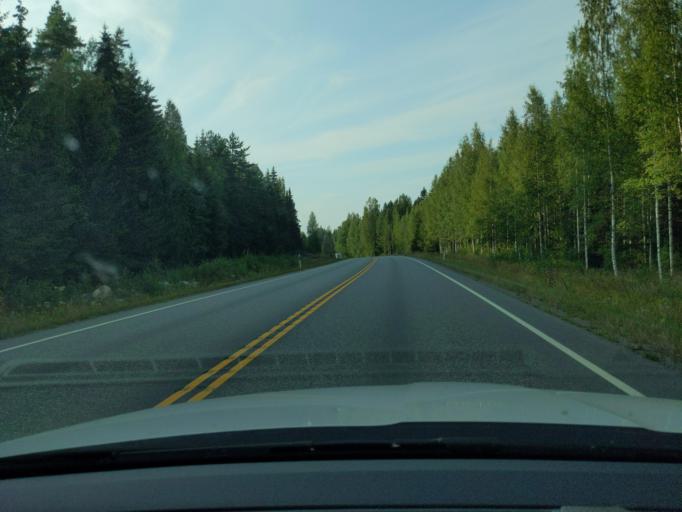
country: FI
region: Paijanne Tavastia
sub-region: Lahti
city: Padasjoki
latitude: 61.3330
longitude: 25.2686
